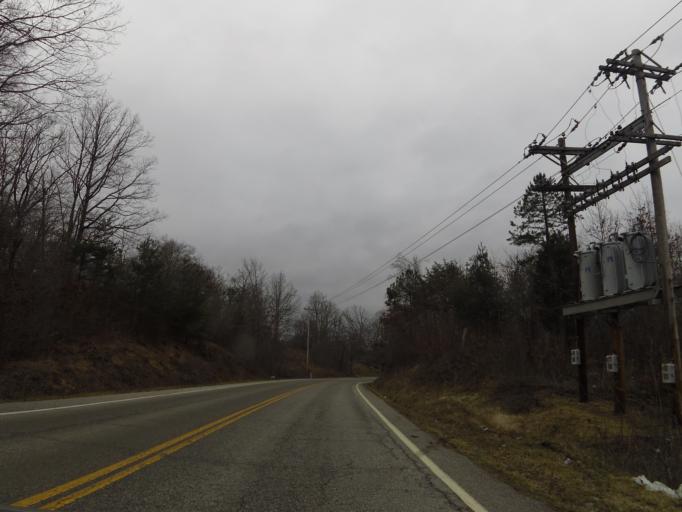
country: US
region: Tennessee
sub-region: Scott County
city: Huntsville
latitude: 36.3036
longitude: -84.6297
